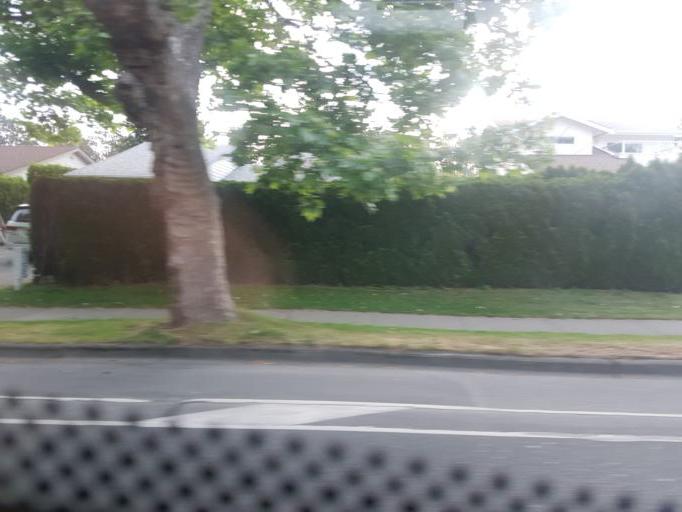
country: CA
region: British Columbia
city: Oak Bay
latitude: 48.4792
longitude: -123.3357
